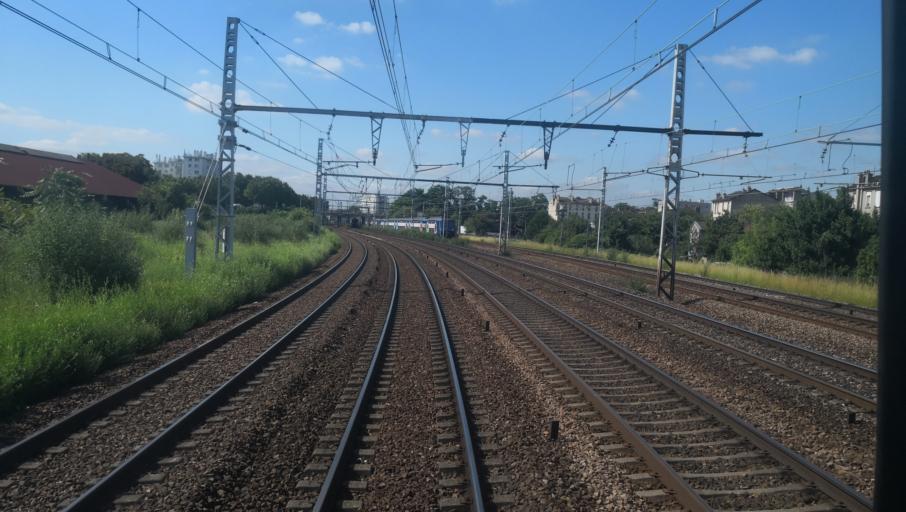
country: FR
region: Ile-de-France
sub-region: Departement du Val-de-Marne
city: Alfortville
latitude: 48.7976
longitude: 2.4293
